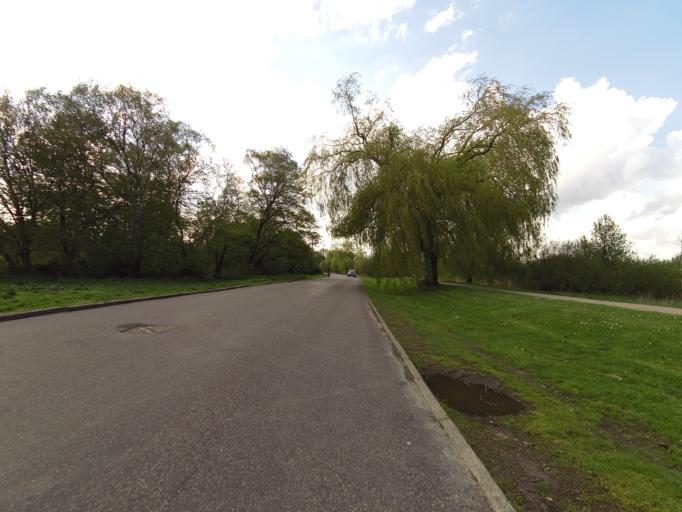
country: DK
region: Capital Region
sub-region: Frederiksberg Kommune
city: Frederiksberg
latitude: 55.7173
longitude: 12.5158
